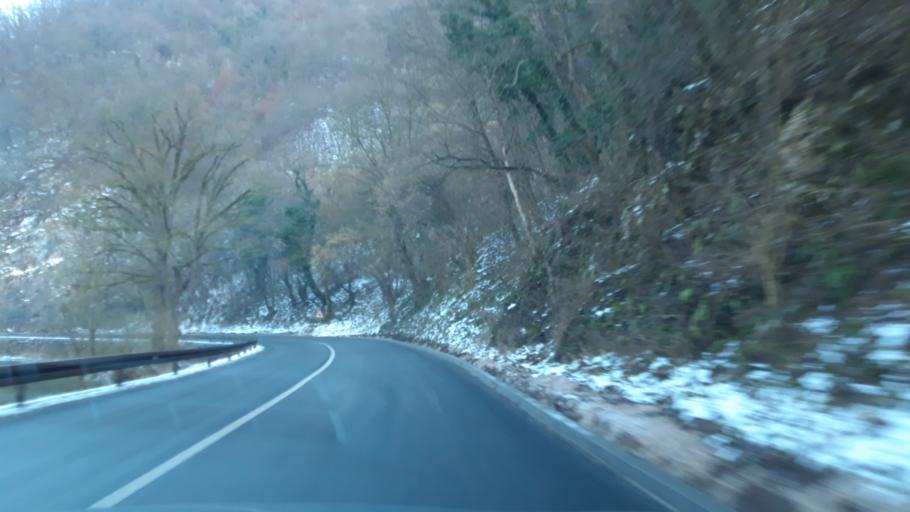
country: RS
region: Central Serbia
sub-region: Macvanski Okrug
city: Mali Zvornik
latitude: 44.2784
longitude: 19.1111
